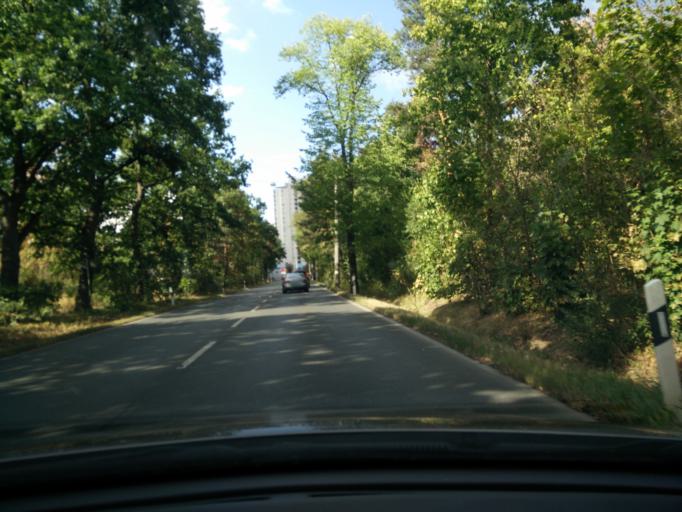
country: DE
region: Bavaria
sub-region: Regierungsbezirk Mittelfranken
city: Stein
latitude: 49.3898
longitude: 11.0333
